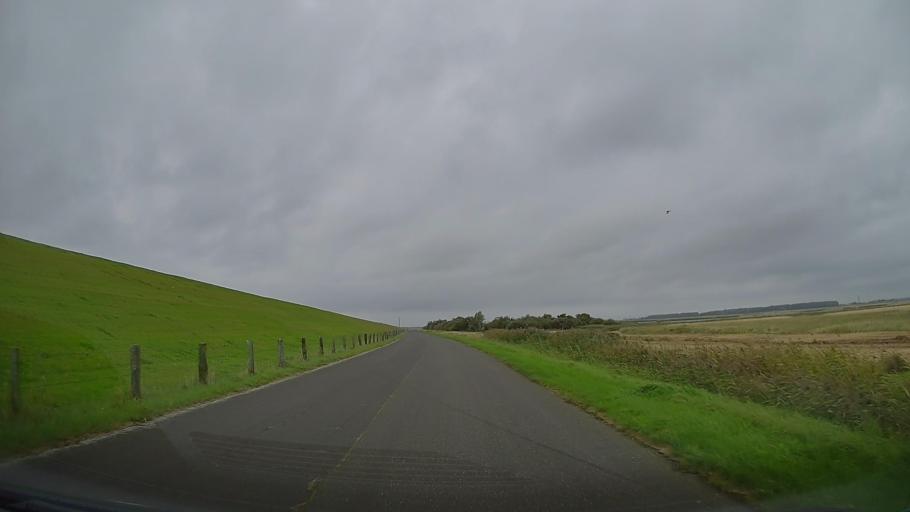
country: DE
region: Schleswig-Holstein
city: Busenwurth
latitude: 54.0459
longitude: 8.9829
